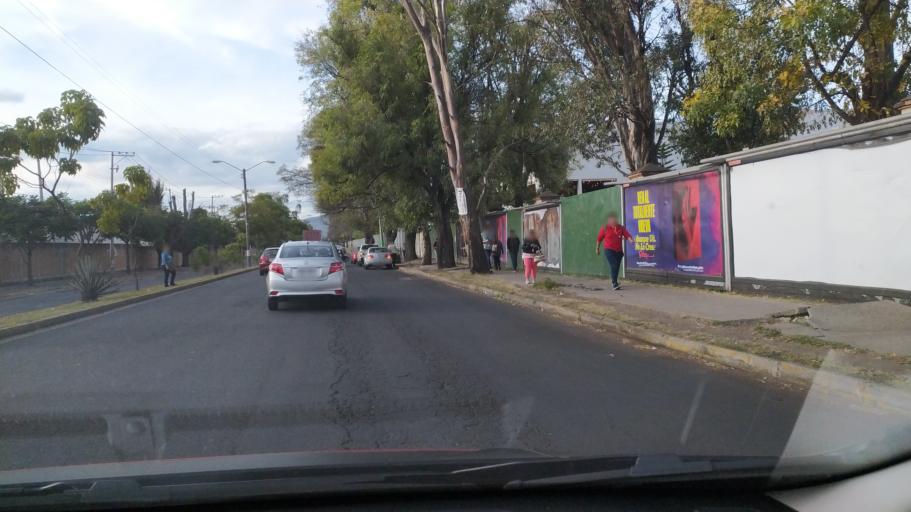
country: MX
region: Jalisco
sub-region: Tlajomulco de Zuniga
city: La Tijera
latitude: 20.6127
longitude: -103.4170
